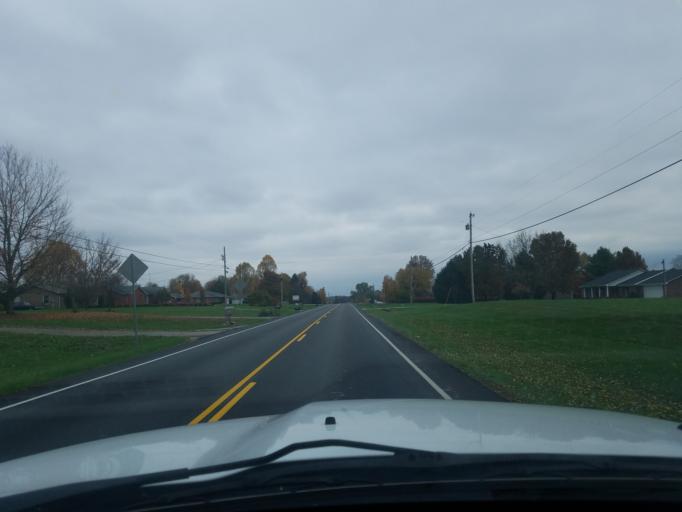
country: US
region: Kentucky
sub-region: Nelson County
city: Bardstown
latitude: 37.7773
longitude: -85.3904
